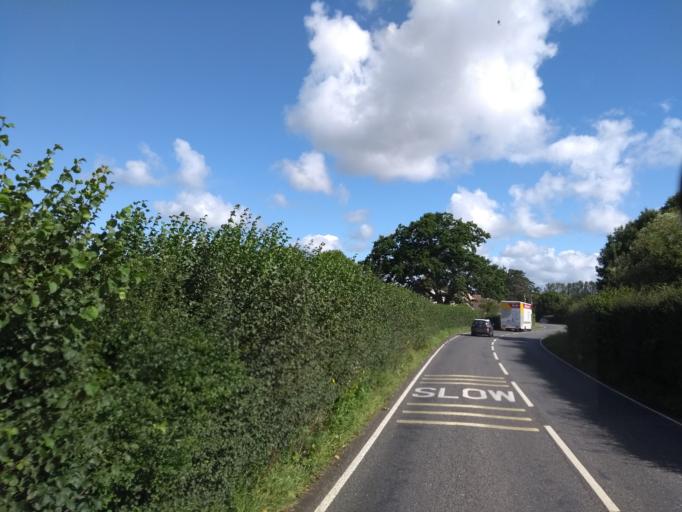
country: GB
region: England
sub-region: Somerset
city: Street
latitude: 51.1187
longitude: -2.7321
